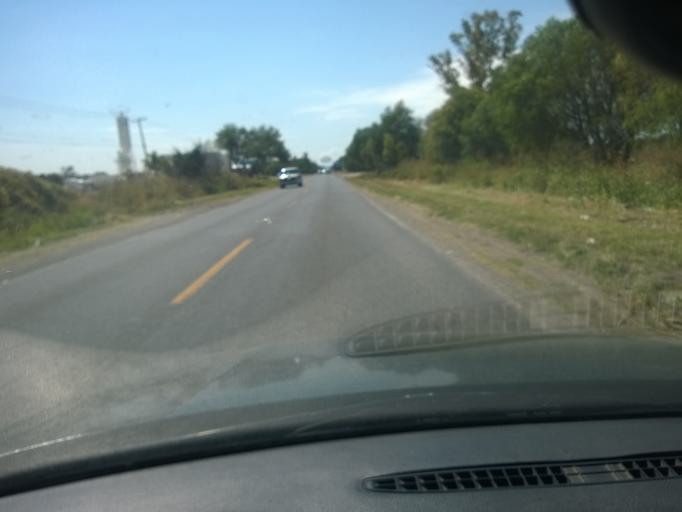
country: MX
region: Guanajuato
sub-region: Leon
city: Plan Guanajuato (La Sandia)
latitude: 20.9699
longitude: -101.7030
